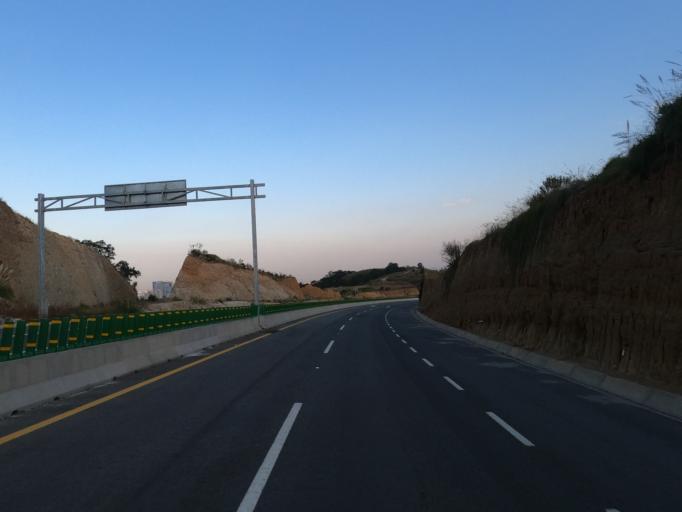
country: MX
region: Mexico
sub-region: Naucalpan de Juarez
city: Llano de las Flores (Barrio del Hueso)
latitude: 19.4223
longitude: -99.3207
